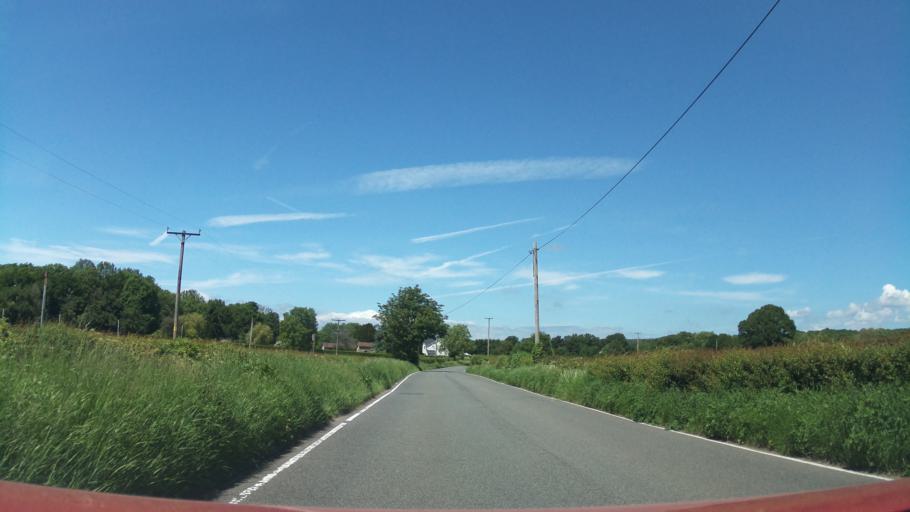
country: GB
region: Wales
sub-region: Monmouthshire
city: Caldicot
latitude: 51.6018
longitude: -2.7376
